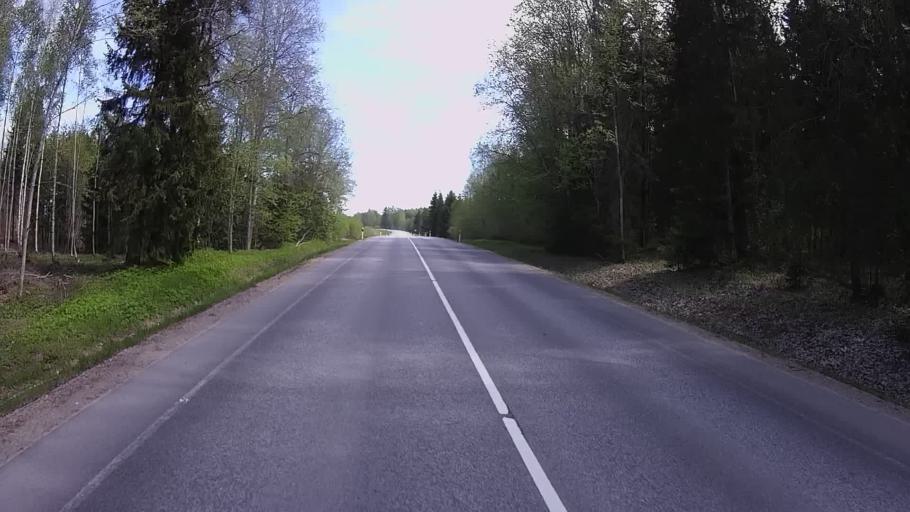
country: EE
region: Valgamaa
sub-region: Valga linn
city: Valga
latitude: 57.7138
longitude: 26.2116
